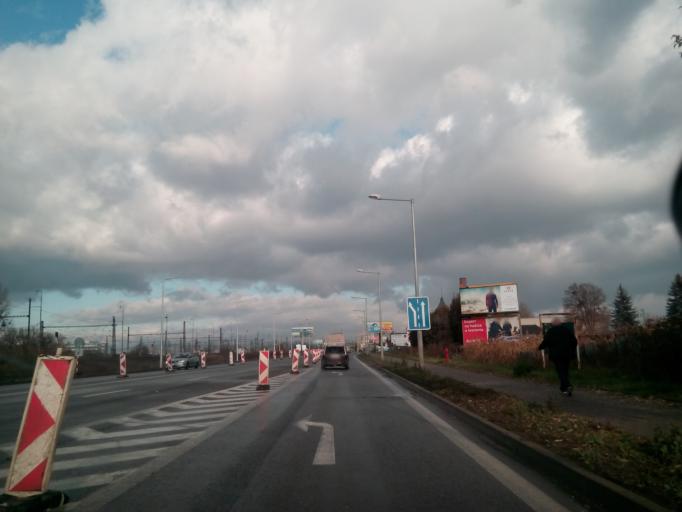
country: SK
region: Presovsky
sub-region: Okres Presov
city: Presov
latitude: 48.9749
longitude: 21.2523
